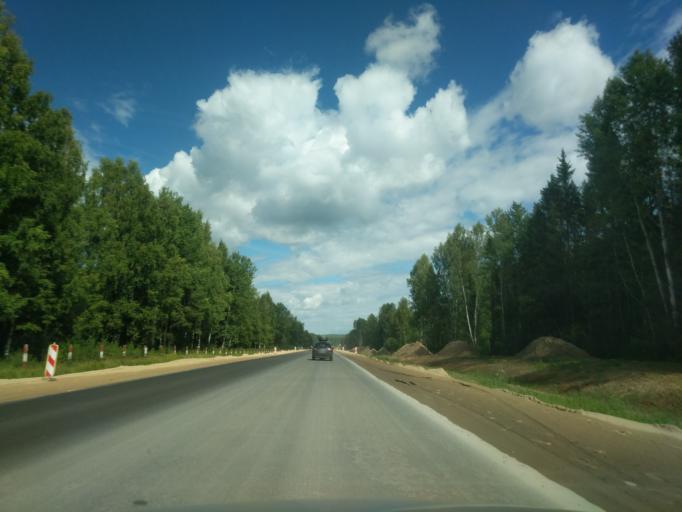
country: RU
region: Jaroslavl
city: Levashevo
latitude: 57.6610
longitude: 40.5690
